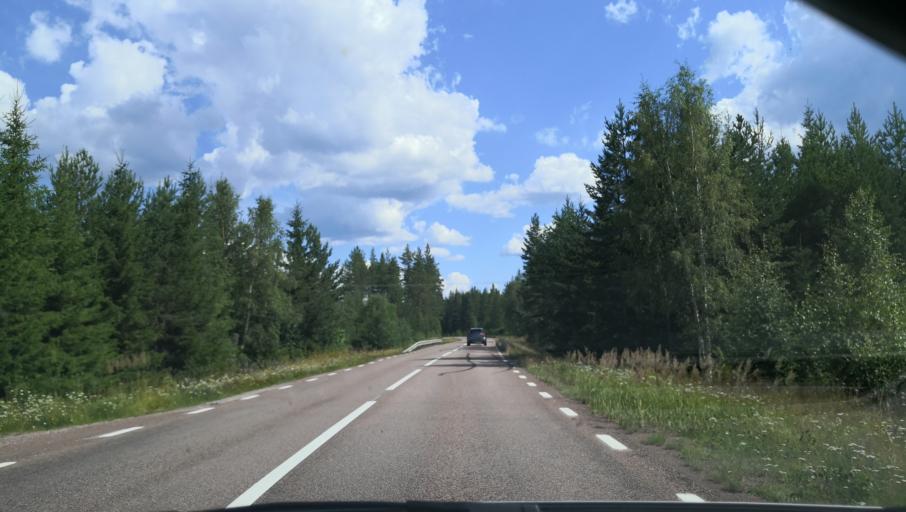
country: SE
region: Dalarna
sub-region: Rattviks Kommun
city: Vikarbyn
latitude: 61.1434
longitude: 15.1202
